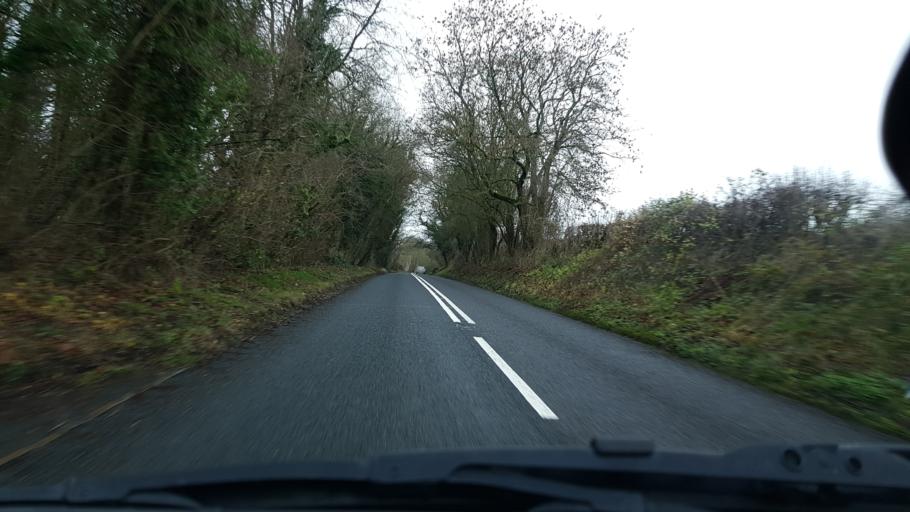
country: GB
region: England
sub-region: Gloucestershire
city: Charlton Kings
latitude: 51.8238
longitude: -2.0332
